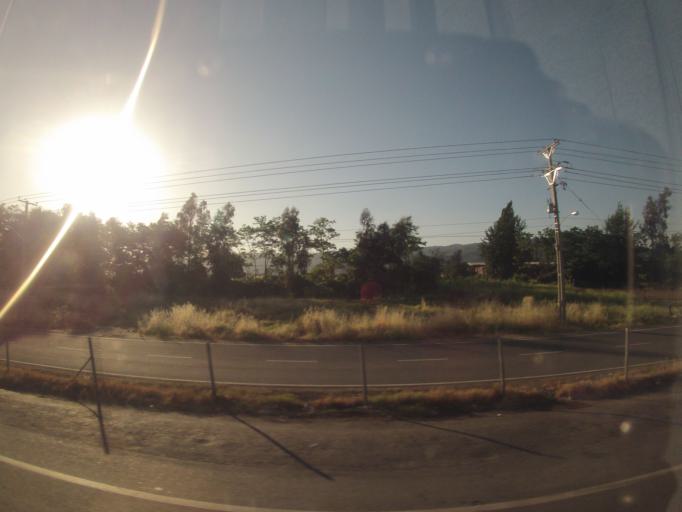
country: CL
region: O'Higgins
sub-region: Provincia de Colchagua
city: Chimbarongo
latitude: -34.7178
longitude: -71.0321
